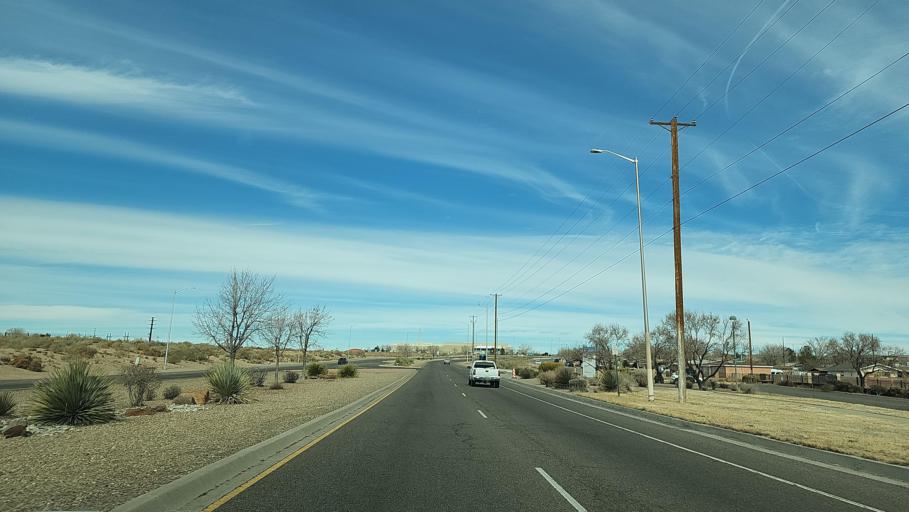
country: US
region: New Mexico
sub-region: Bernalillo County
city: Albuquerque
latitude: 35.0722
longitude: -106.7127
